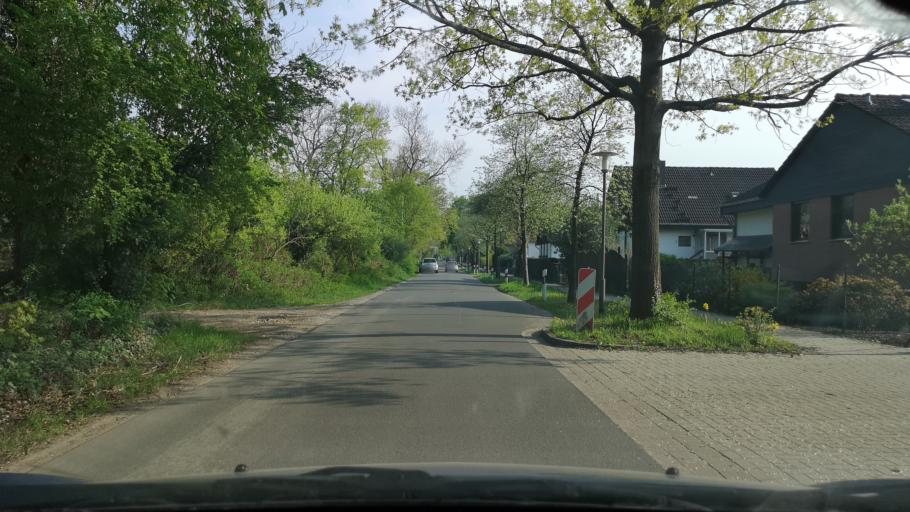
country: DE
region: Lower Saxony
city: Garbsen-Mitte
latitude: 52.4469
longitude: 9.6520
